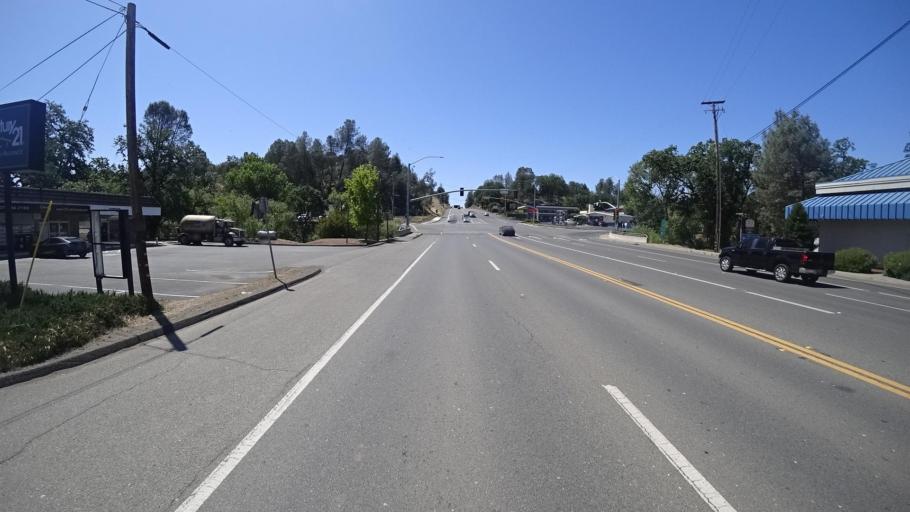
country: US
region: California
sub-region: Lake County
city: Lower Lake
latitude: 38.9109
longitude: -122.6122
